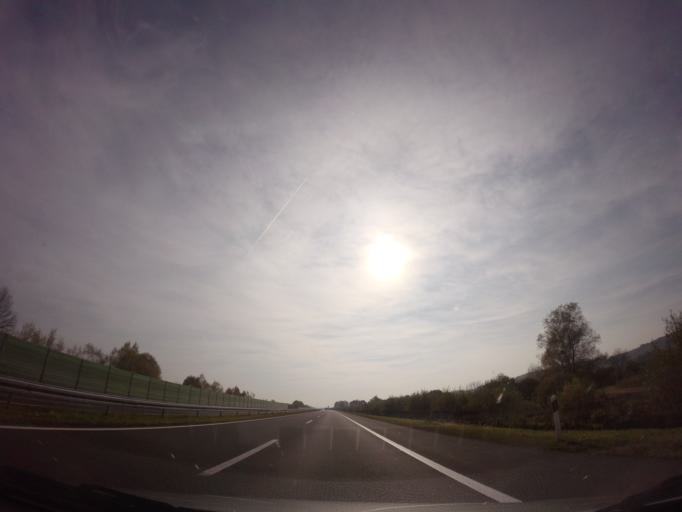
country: HR
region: Varazdinska
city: Remetinec
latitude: 46.0322
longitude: 16.2951
